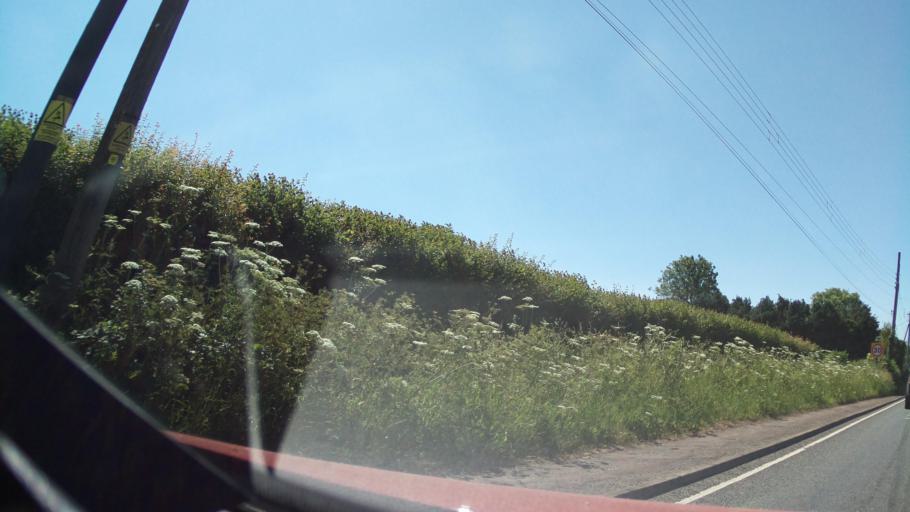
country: GB
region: England
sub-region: Bath and North East Somerset
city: Clutton
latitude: 51.3009
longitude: -2.5334
